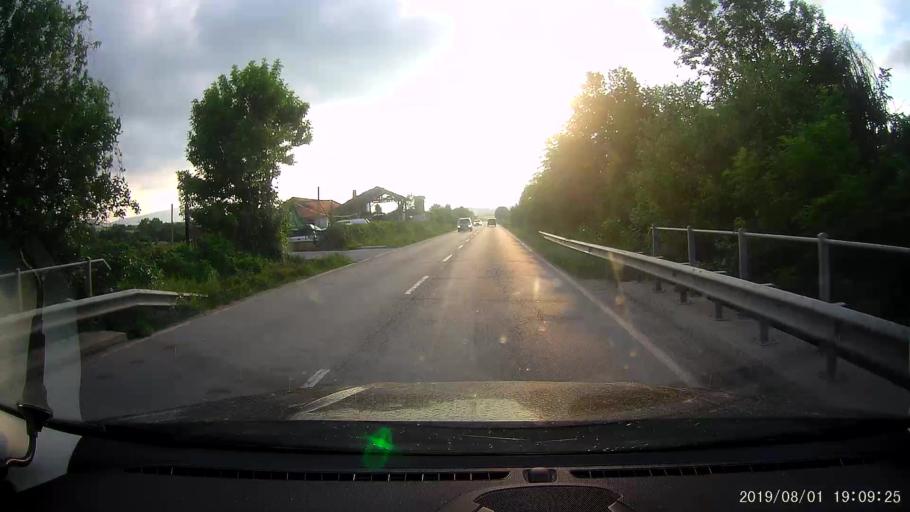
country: BG
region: Shumen
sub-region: Obshtina Smyadovo
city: Smyadovo
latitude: 42.9842
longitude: 27.0044
